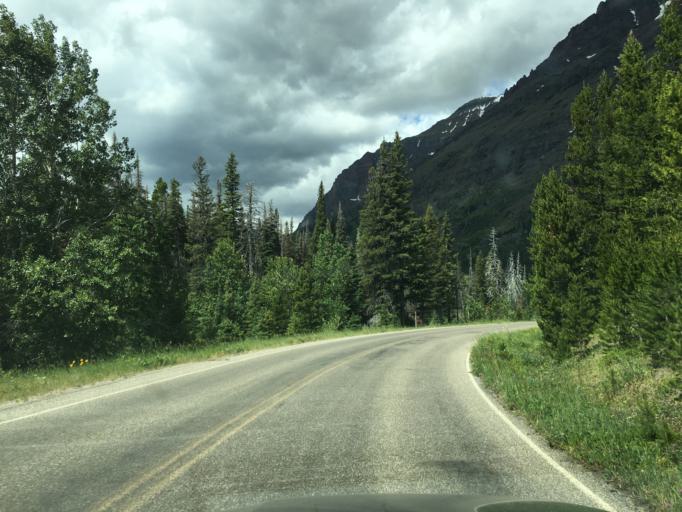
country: US
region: Montana
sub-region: Glacier County
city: South Browning
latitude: 48.4851
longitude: -113.3634
